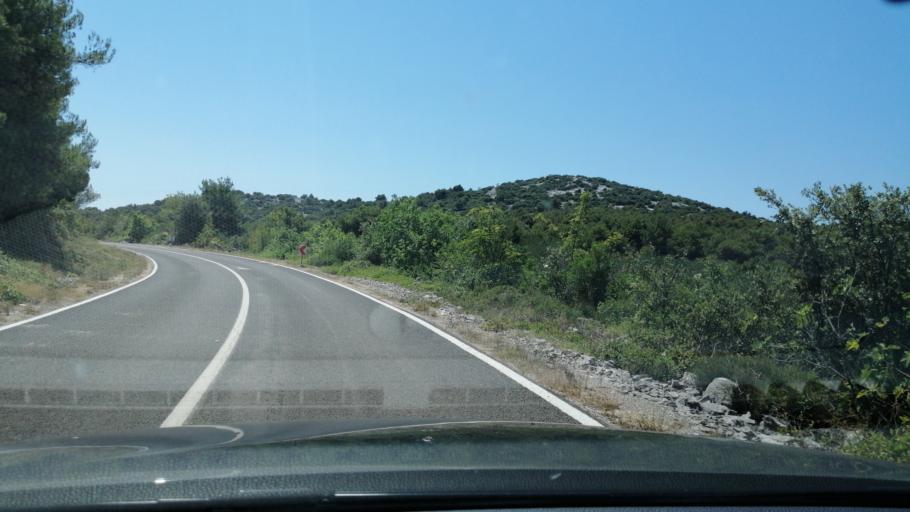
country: HR
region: Sibensko-Kniniska
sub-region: Grad Sibenik
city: Pirovac
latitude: 43.8454
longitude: 15.6864
